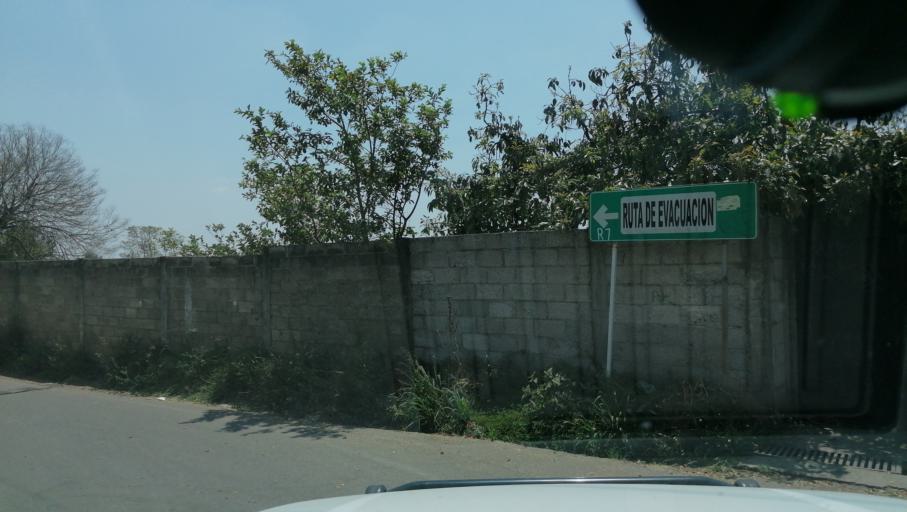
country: MX
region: Puebla
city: Atlixco
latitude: 18.8754
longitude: -98.4875
